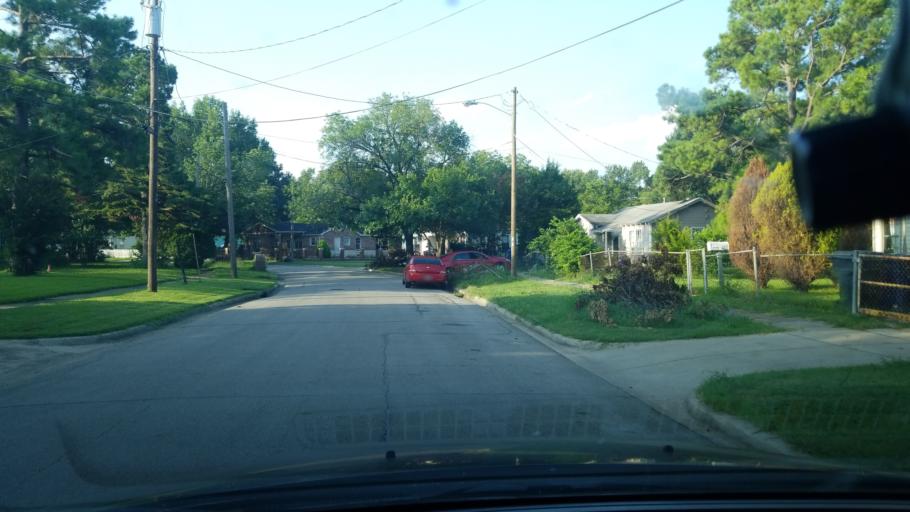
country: US
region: Texas
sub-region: Dallas County
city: Balch Springs
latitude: 32.7136
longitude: -96.6765
